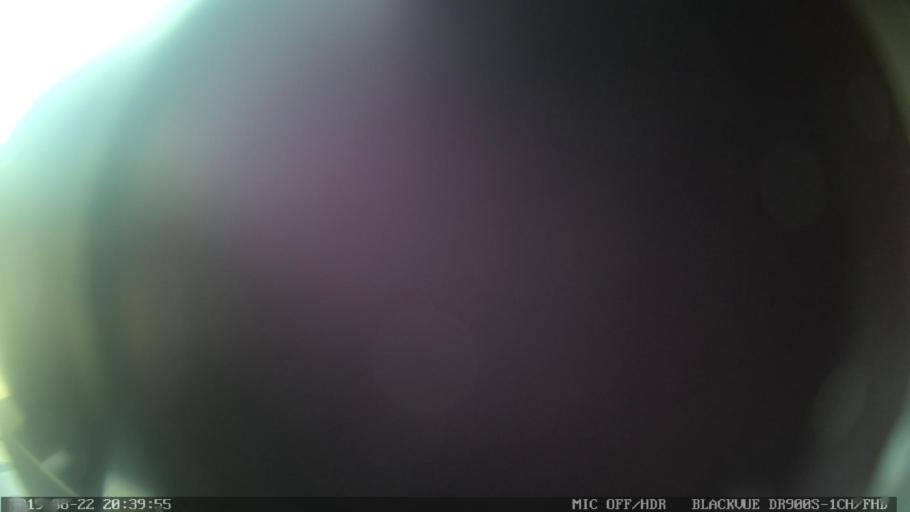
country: PT
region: Castelo Branco
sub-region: Proenca-A-Nova
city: Proenca-a-Nova
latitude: 39.6879
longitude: -7.7796
